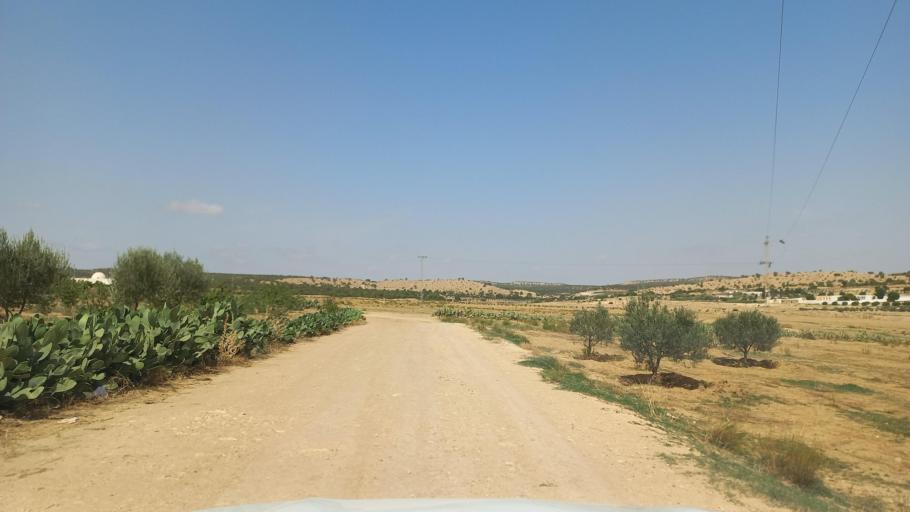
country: TN
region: Al Qasrayn
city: Sbiba
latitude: 35.3880
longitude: 8.9585
